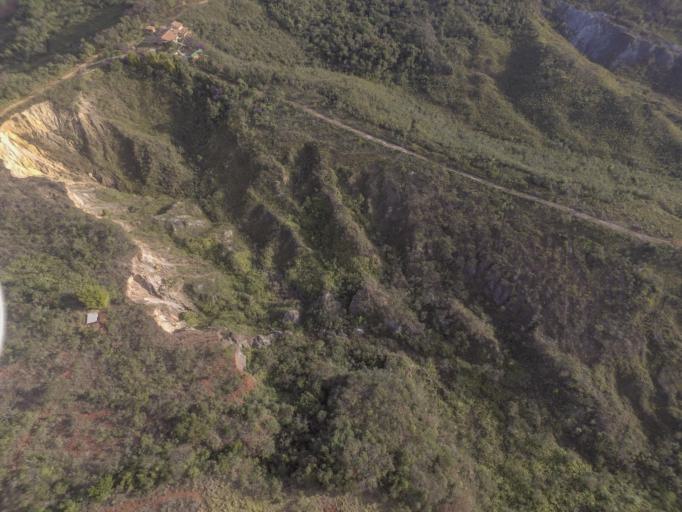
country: BR
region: Minas Gerais
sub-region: Tiradentes
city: Tiradentes
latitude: -21.0565
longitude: -44.1020
